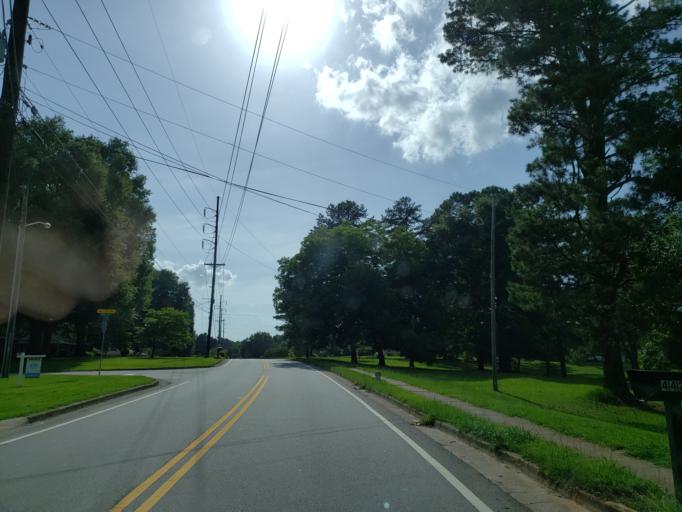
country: US
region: Georgia
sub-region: Cobb County
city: Powder Springs
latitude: 33.8751
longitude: -84.6810
